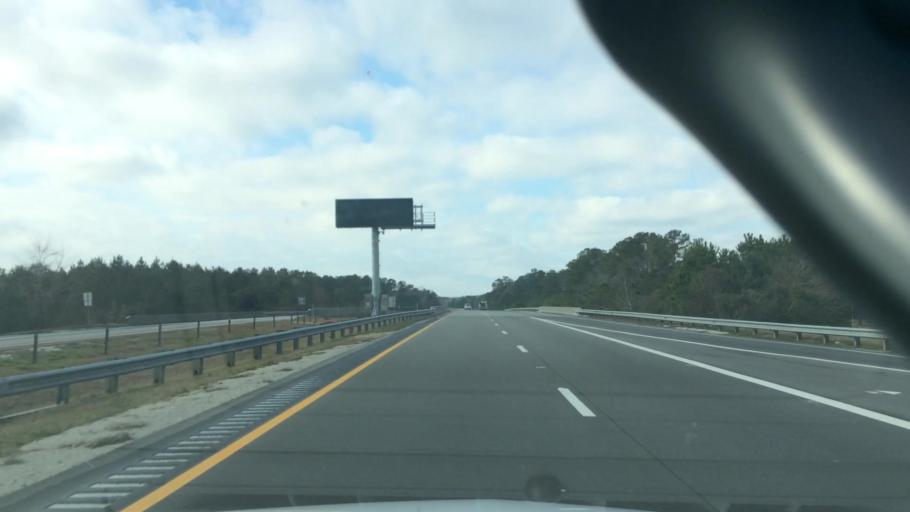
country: US
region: North Carolina
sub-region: New Hanover County
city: Wrightsboro
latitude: 34.3171
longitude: -77.9213
